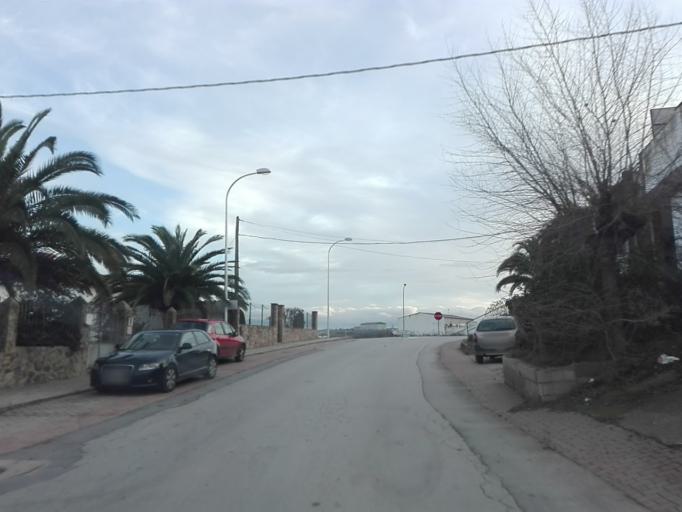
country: ES
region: Extremadura
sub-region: Provincia de Badajoz
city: Usagre
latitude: 38.3536
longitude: -6.1709
